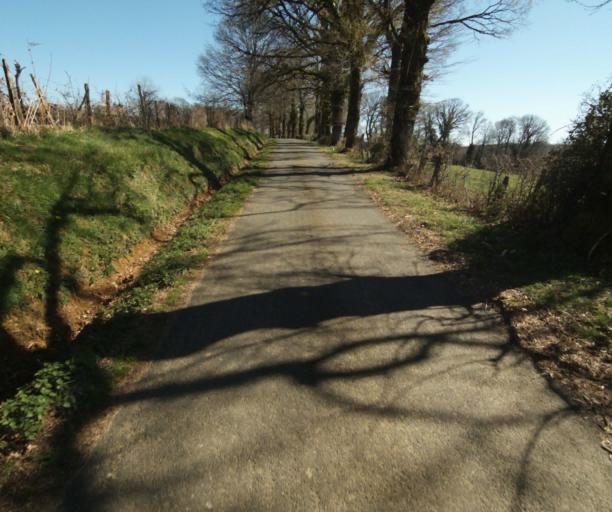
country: FR
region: Limousin
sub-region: Departement de la Correze
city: Seilhac
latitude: 45.3864
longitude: 1.6769
